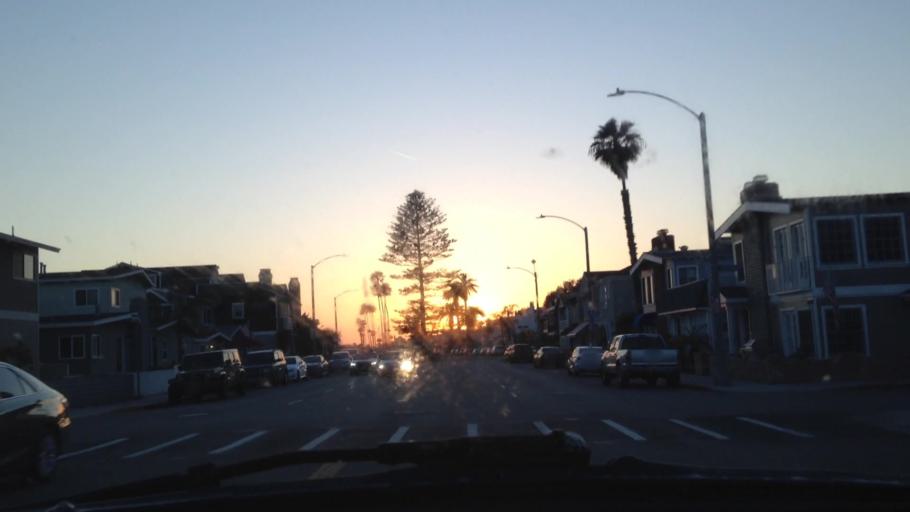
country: US
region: California
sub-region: Orange County
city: Newport Beach
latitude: 33.6033
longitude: -117.9036
